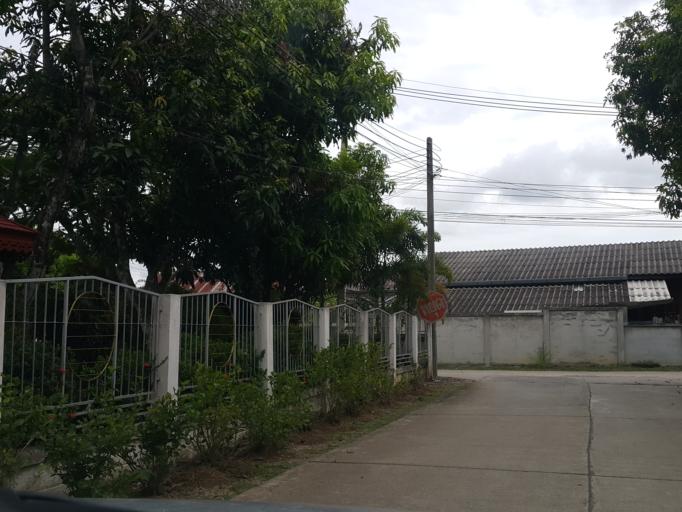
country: TH
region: Chiang Mai
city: San Sai
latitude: 18.8403
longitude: 99.1225
